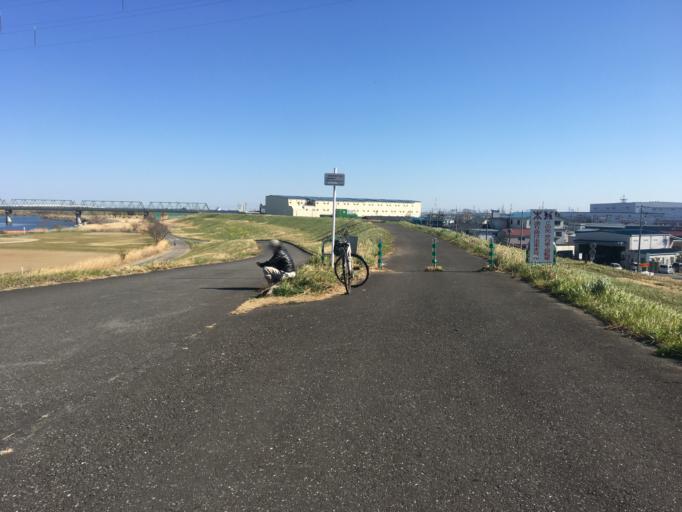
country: JP
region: Saitama
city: Shiki
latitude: 35.8327
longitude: 139.6053
